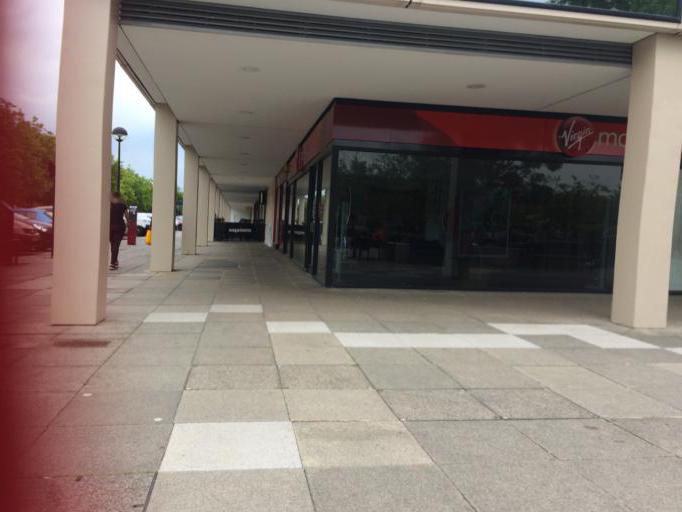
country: GB
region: England
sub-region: Milton Keynes
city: Milton Keynes
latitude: 52.0425
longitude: -0.7597
